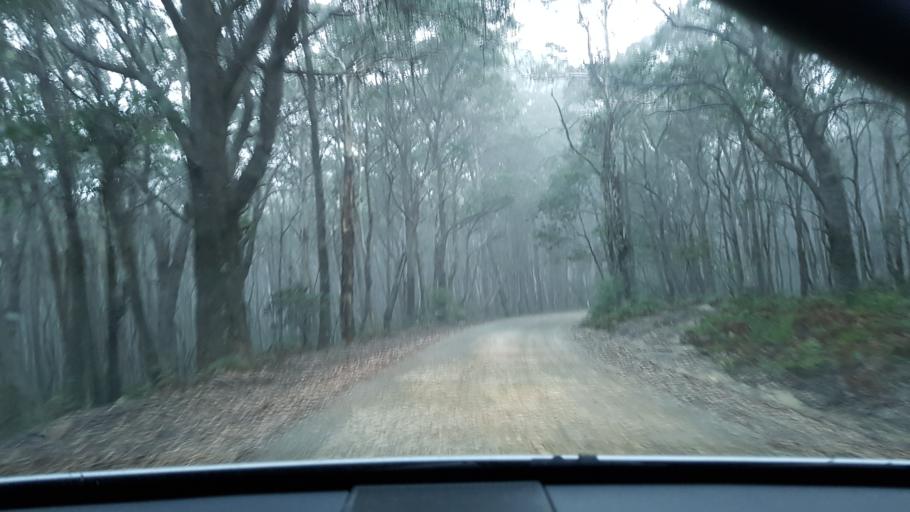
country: AU
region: New South Wales
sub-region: Blue Mountains Municipality
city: Katoomba
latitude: -33.9936
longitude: 150.0738
